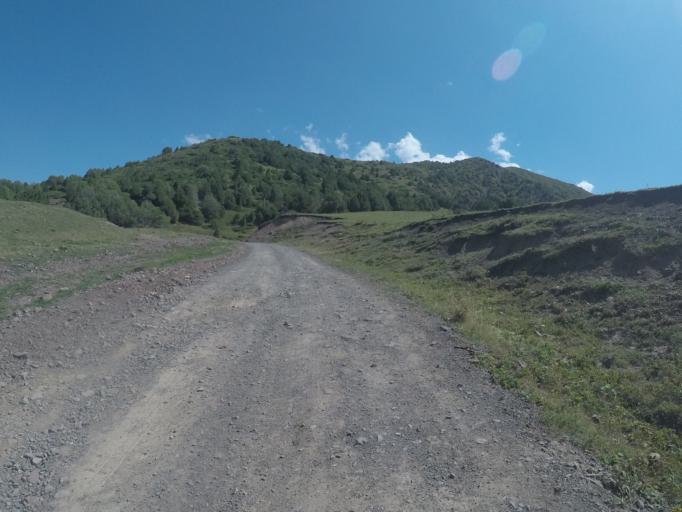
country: KG
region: Chuy
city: Bishkek
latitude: 42.6467
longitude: 74.5584
